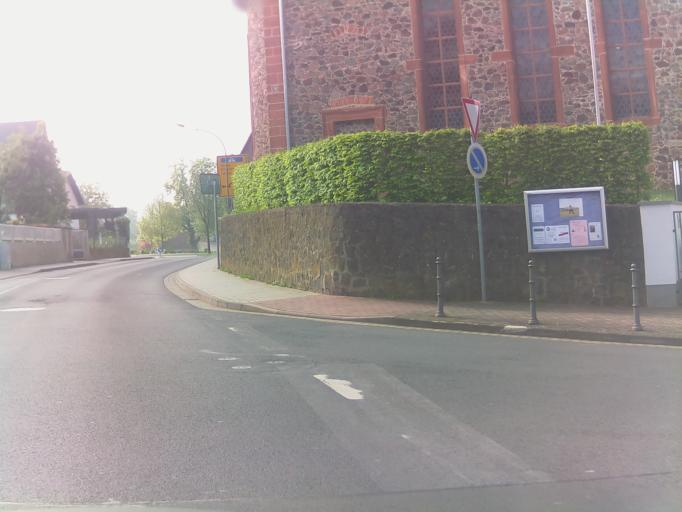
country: DE
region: Hesse
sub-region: Regierungsbezirk Darmstadt
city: Hammersbach
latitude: 50.1888
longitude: 8.9948
